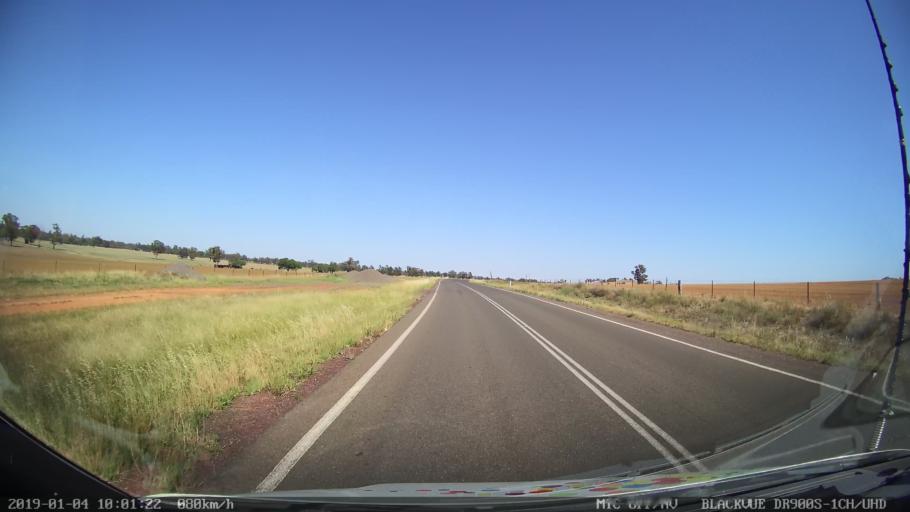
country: AU
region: New South Wales
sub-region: Cabonne
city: Canowindra
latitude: -33.4877
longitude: 148.3719
